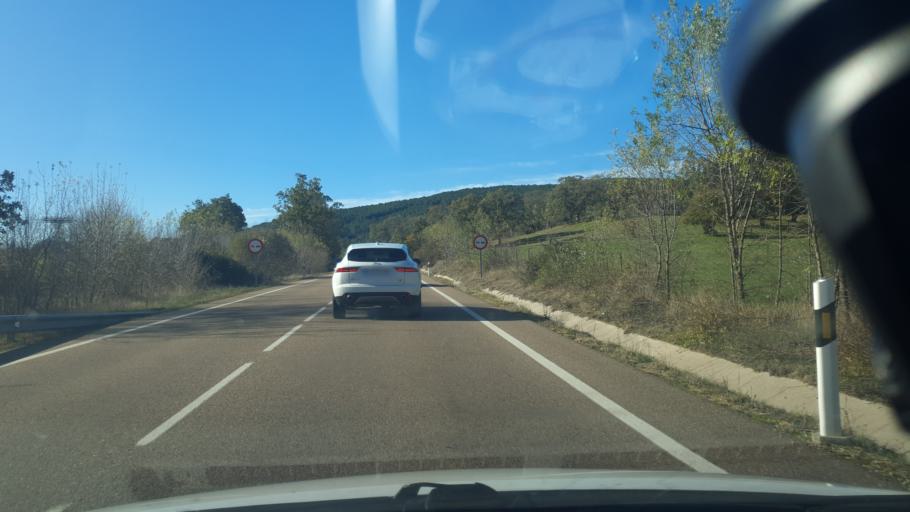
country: ES
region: Castille and Leon
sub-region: Provincia de Avila
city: Arenas de San Pedro
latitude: 40.1868
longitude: -5.0808
